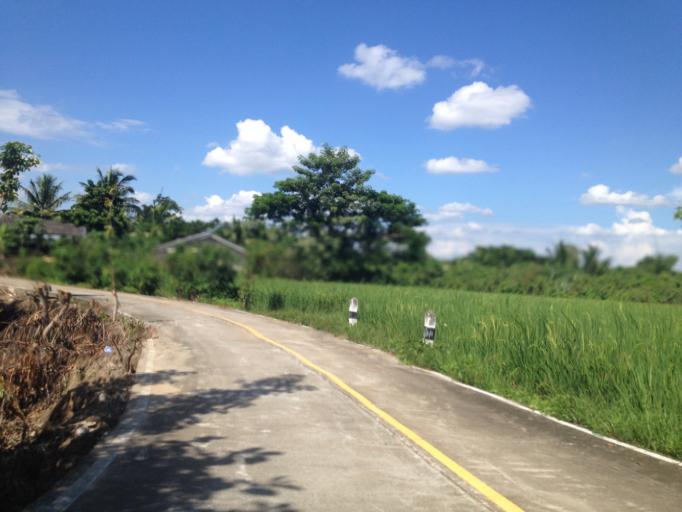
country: TH
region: Chiang Mai
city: Saraphi
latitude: 18.6957
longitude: 98.9815
